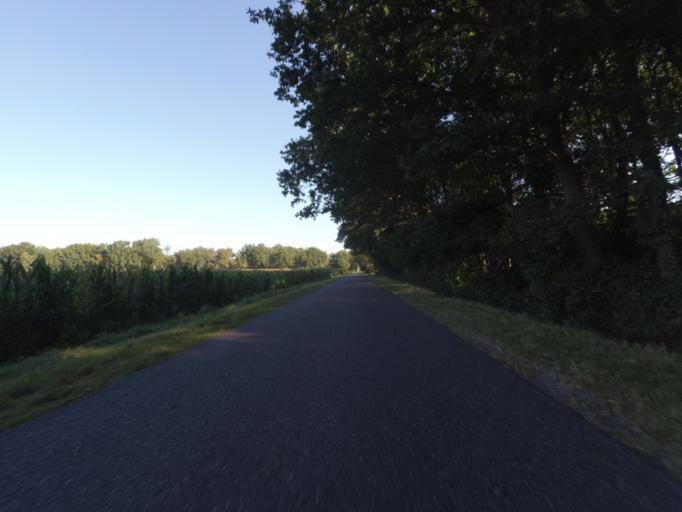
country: NL
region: Gelderland
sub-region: Gemeente Barneveld
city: Voorthuizen
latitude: 52.1887
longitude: 5.5657
